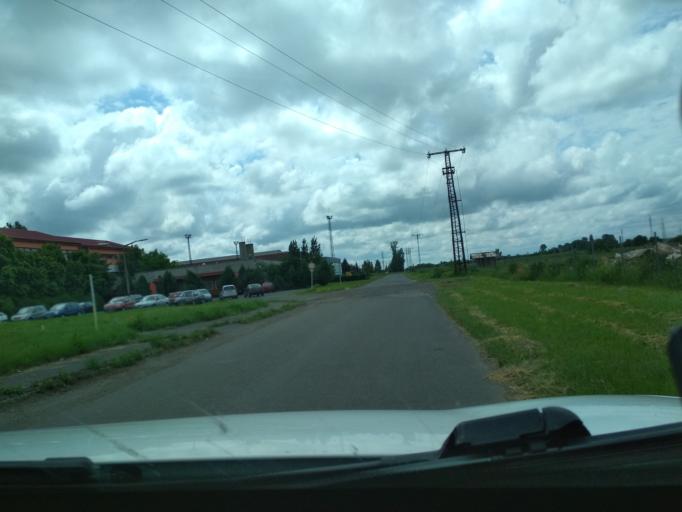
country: HU
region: Jasz-Nagykun-Szolnok
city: Tiszafured
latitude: 47.6097
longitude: 20.7321
